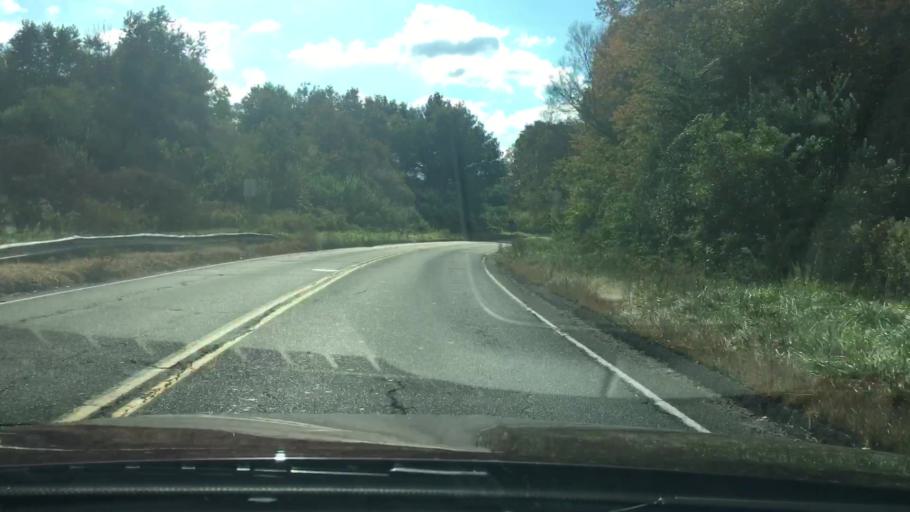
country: US
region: Connecticut
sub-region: New Haven County
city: Meriden
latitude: 41.4917
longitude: -72.7633
